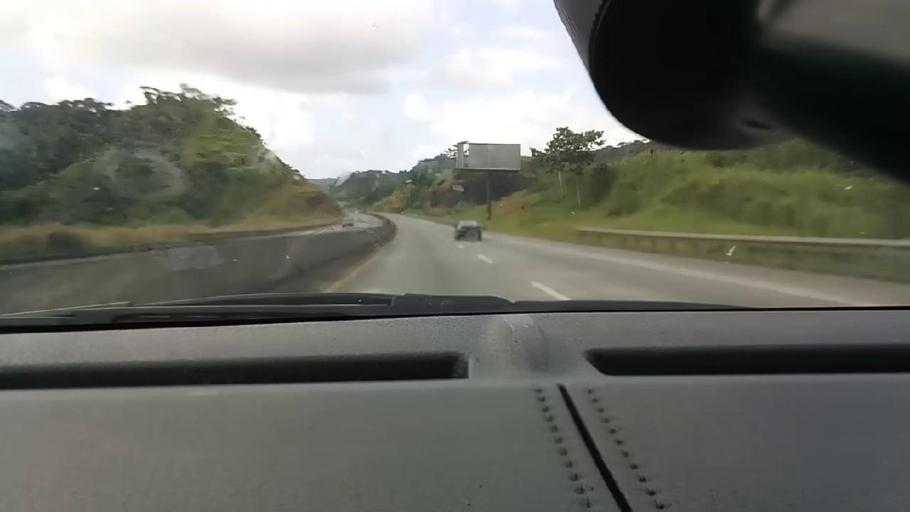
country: PA
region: Colon
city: Gatun
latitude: 9.2837
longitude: -79.7457
